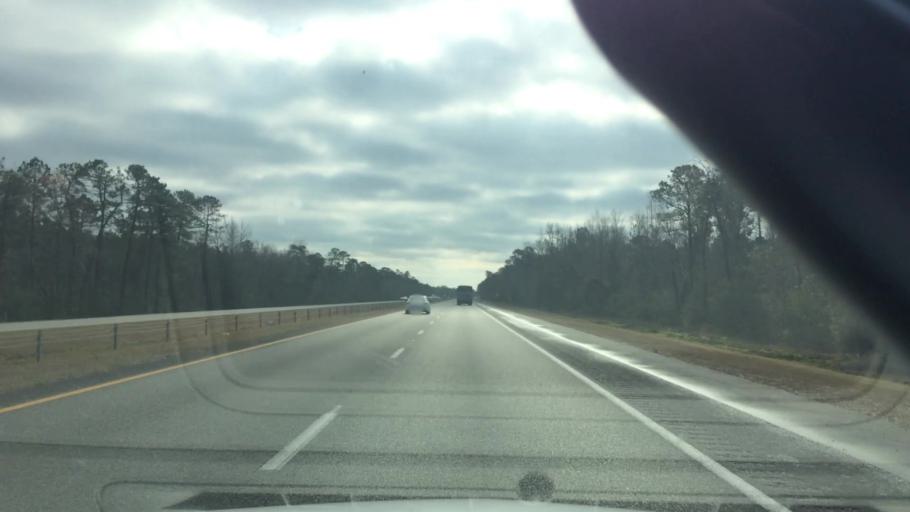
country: US
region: North Carolina
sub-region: Pender County
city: Rocky Point
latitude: 34.4036
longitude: -77.8723
